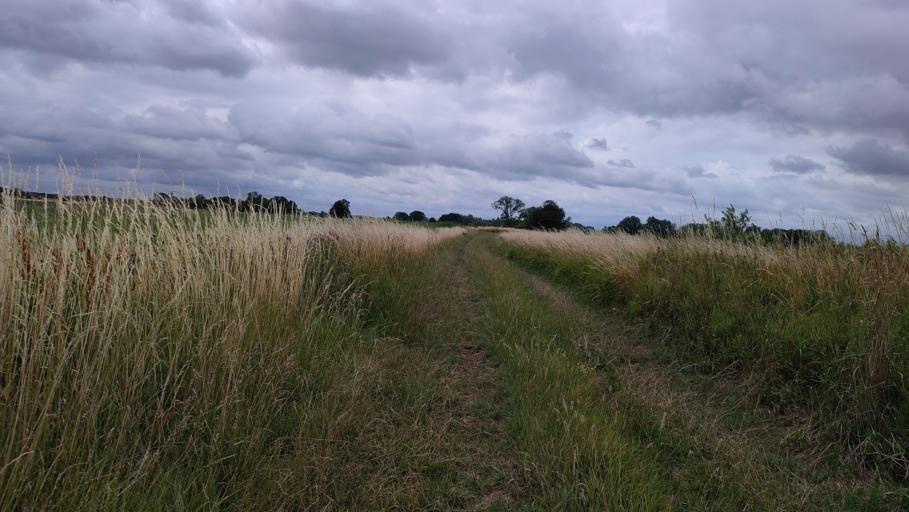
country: DE
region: Lower Saxony
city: Hitzacker
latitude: 53.1618
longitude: 11.1034
